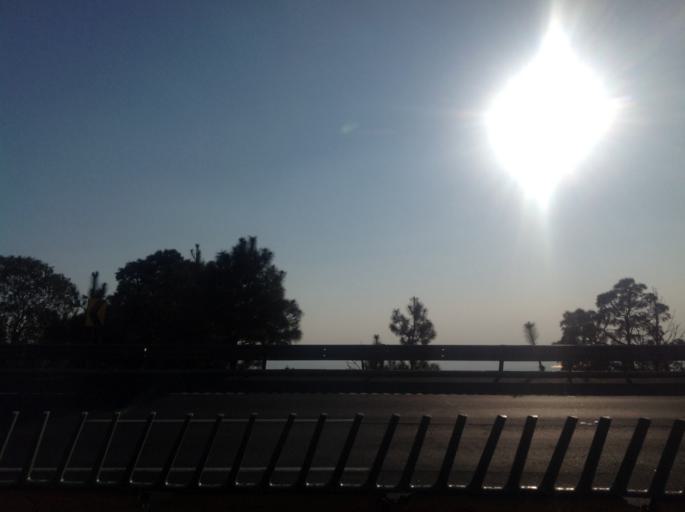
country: MX
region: Mexico
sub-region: Ixtapaluca
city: San Jeronimo Cuatro Vientos
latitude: 19.3007
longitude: -98.7489
